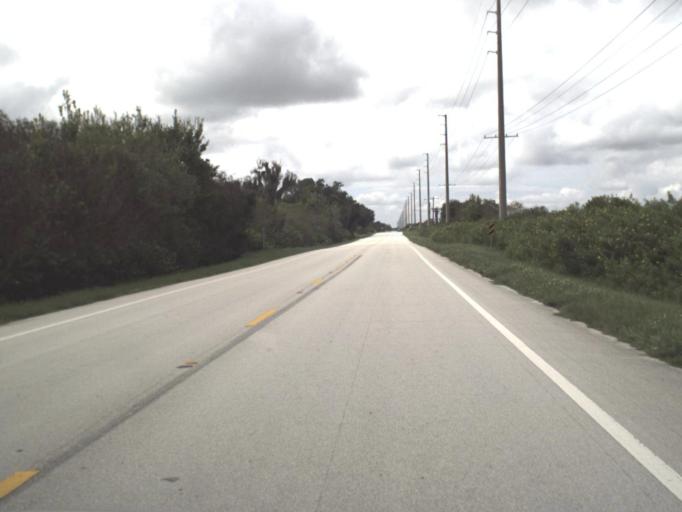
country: US
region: Florida
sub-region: Hardee County
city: Bowling Green
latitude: 27.5950
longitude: -82.0023
